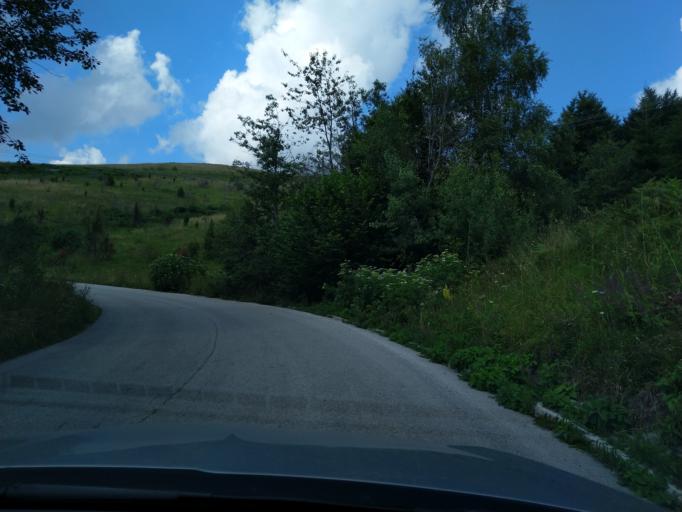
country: RS
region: Central Serbia
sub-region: Zlatiborski Okrug
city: Nova Varos
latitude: 43.5573
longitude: 19.9031
